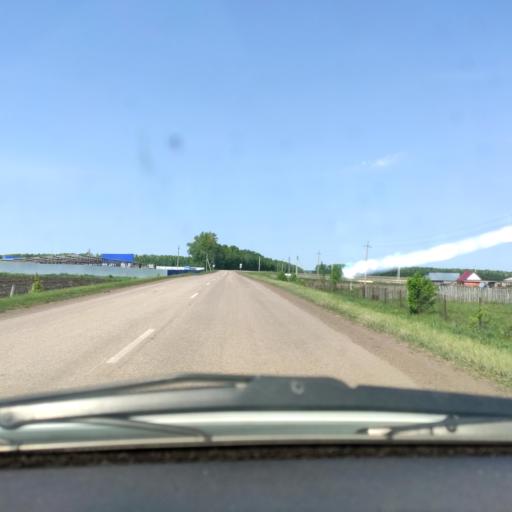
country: RU
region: Bashkortostan
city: Avdon
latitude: 54.5033
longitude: 55.6197
